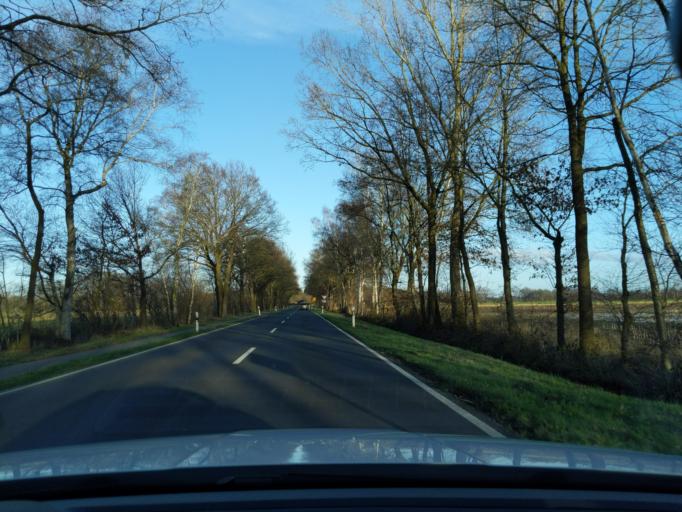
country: DE
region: Lower Saxony
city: Bawinkel
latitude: 52.6591
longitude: 7.3582
